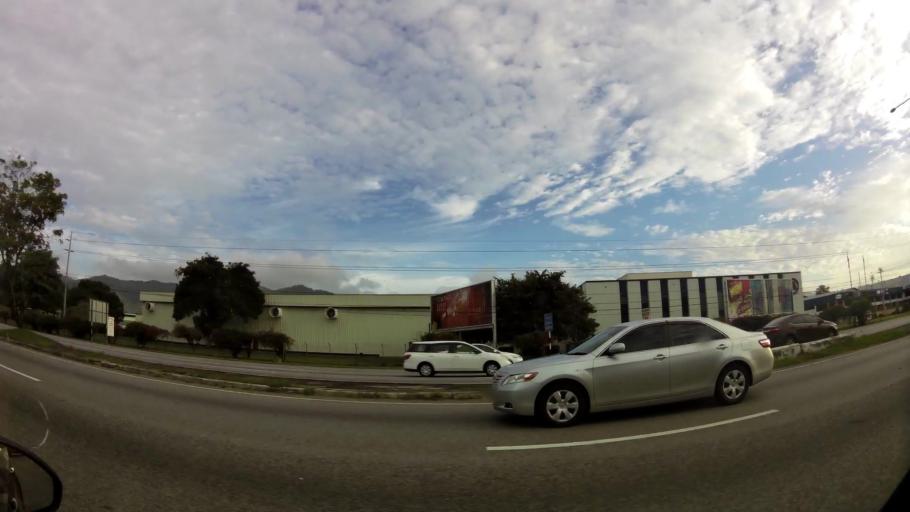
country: TT
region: Tunapuna/Piarco
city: Tunapuna
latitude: 10.6364
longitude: -61.3740
